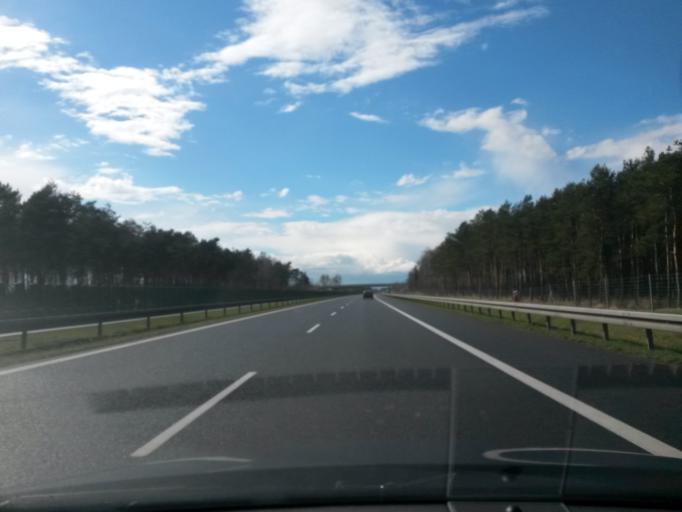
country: PL
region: Greater Poland Voivodeship
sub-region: Powiat slupecki
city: Strzalkowo
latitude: 52.2649
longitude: 17.7488
